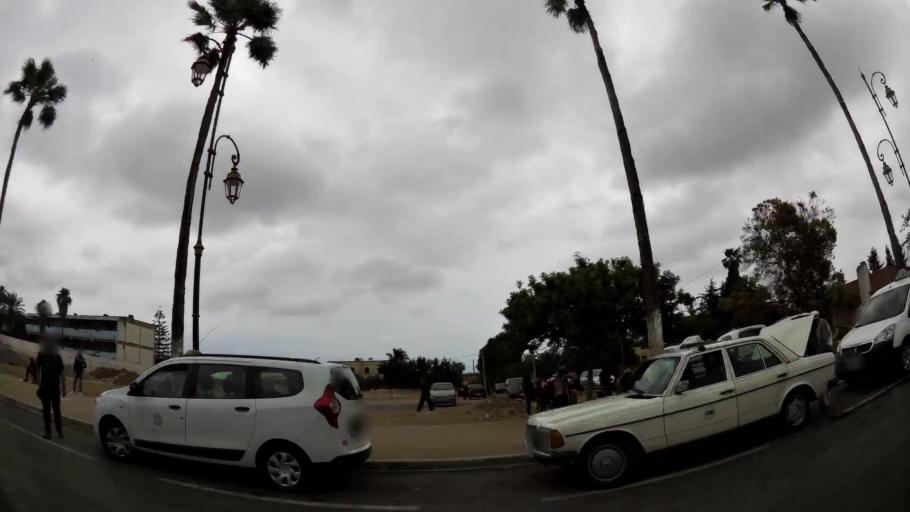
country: MA
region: Rabat-Sale-Zemmour-Zaer
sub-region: Rabat
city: Rabat
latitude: 33.9867
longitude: -6.8203
